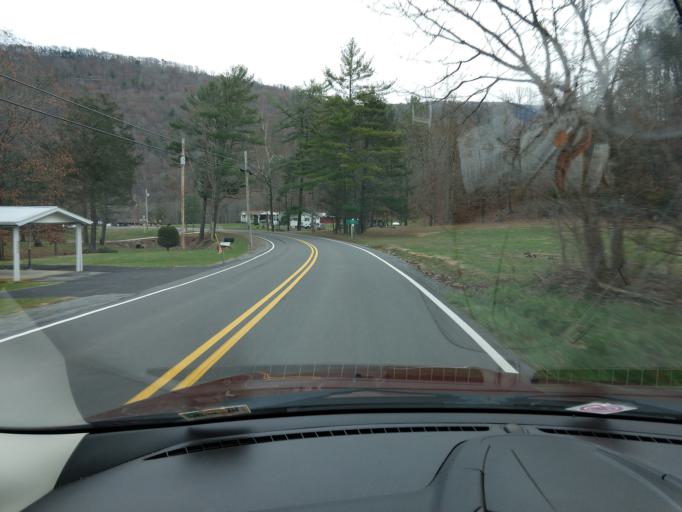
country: US
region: West Virginia
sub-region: Greenbrier County
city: White Sulphur Springs
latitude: 37.7202
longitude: -80.2048
